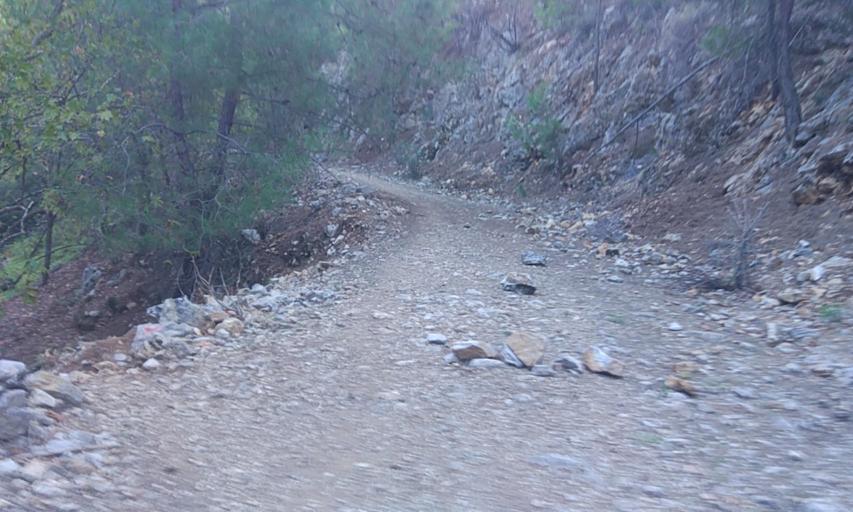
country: TR
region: Antalya
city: Tekirova
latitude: 36.4402
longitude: 30.4407
